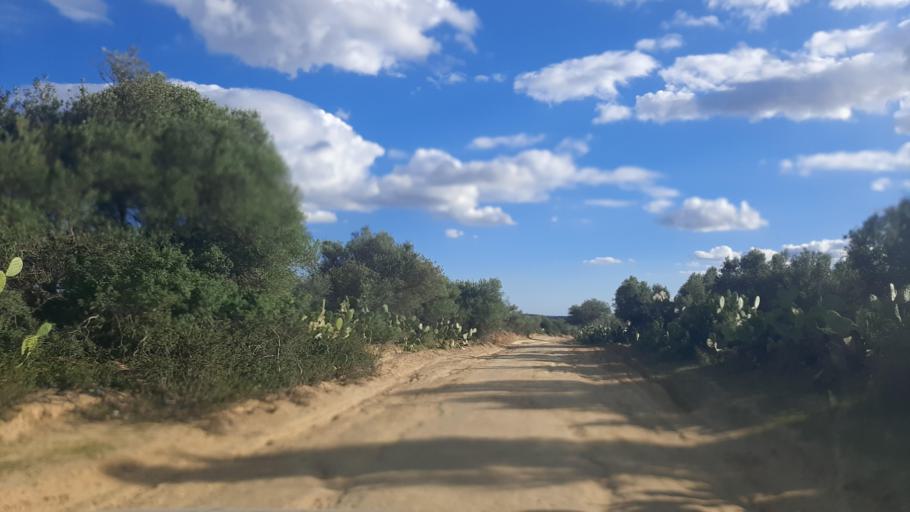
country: TN
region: Nabul
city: Bu `Urqub
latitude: 36.4586
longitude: 10.4930
